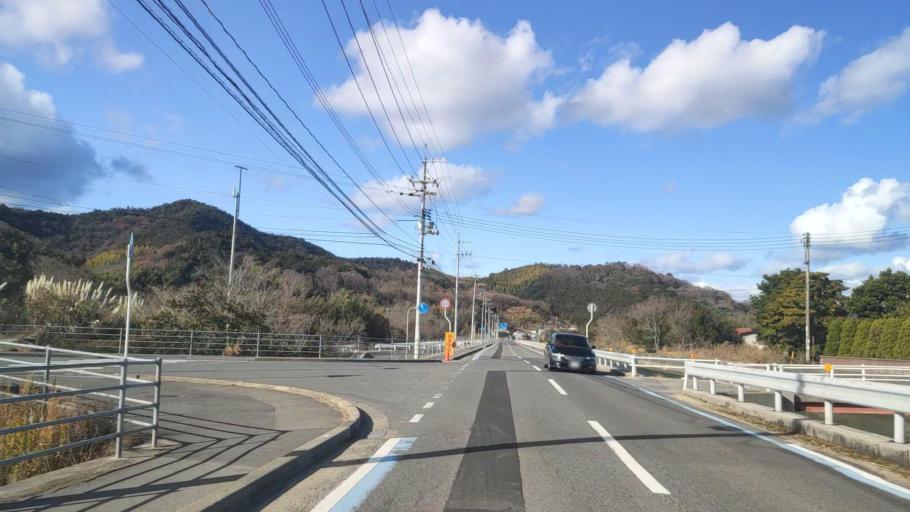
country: JP
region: Hiroshima
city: Innoshima
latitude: 34.2150
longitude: 133.1085
